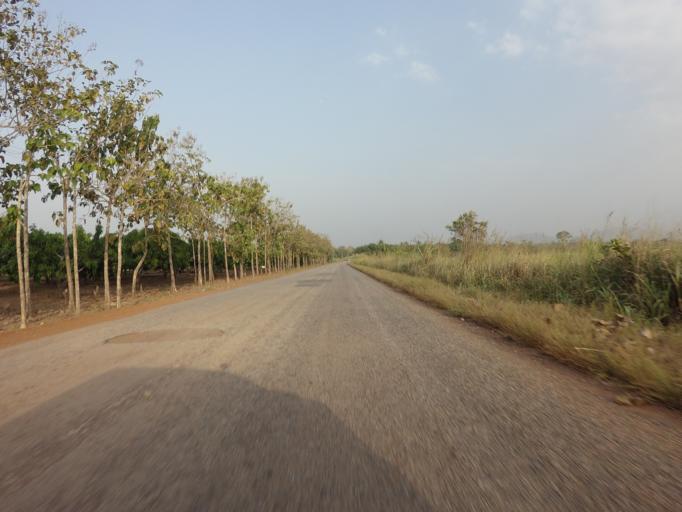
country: GH
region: Volta
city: Ho
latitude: 6.5746
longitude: 0.3151
